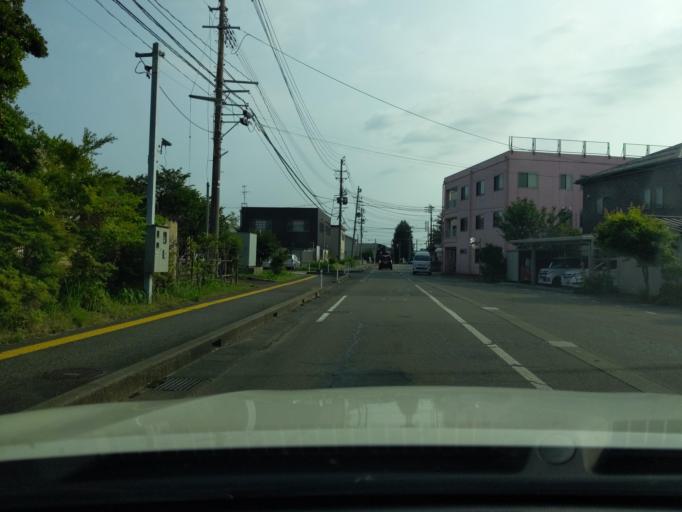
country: JP
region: Niigata
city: Nagaoka
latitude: 37.4504
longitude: 138.8154
